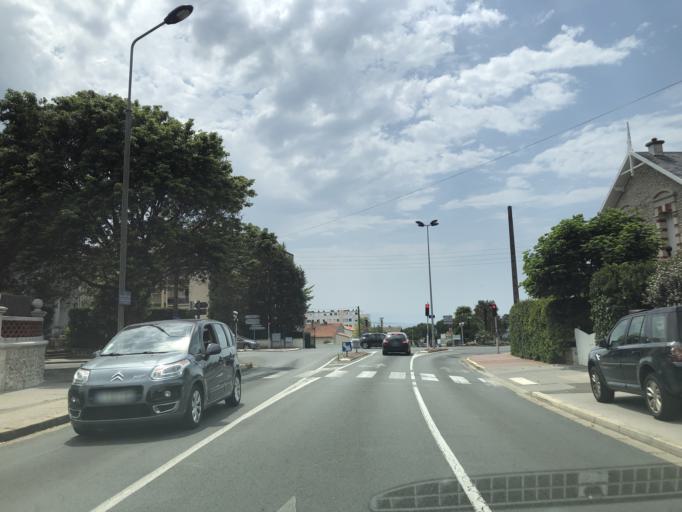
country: FR
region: Poitou-Charentes
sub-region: Departement de la Charente-Maritime
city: Royan
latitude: 45.6247
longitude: -1.0444
